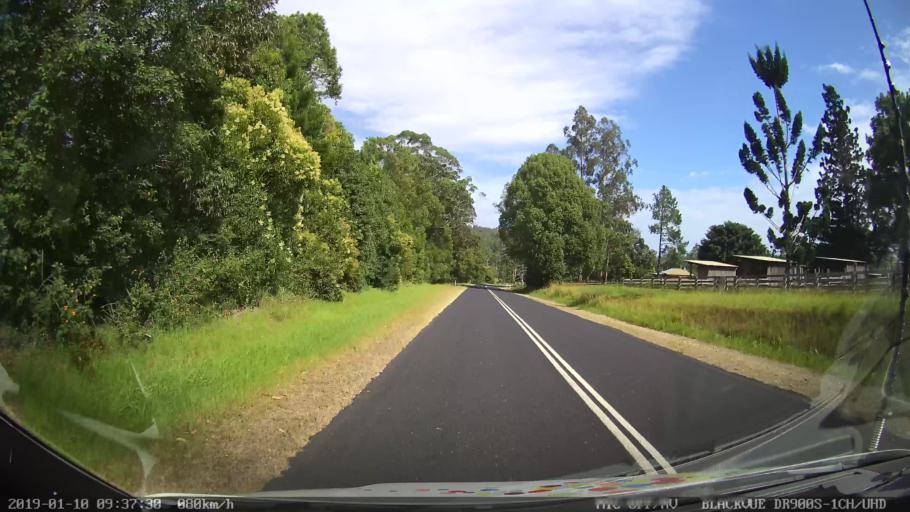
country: AU
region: New South Wales
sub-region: Coffs Harbour
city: Nana Glen
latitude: -30.1871
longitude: 153.0089
